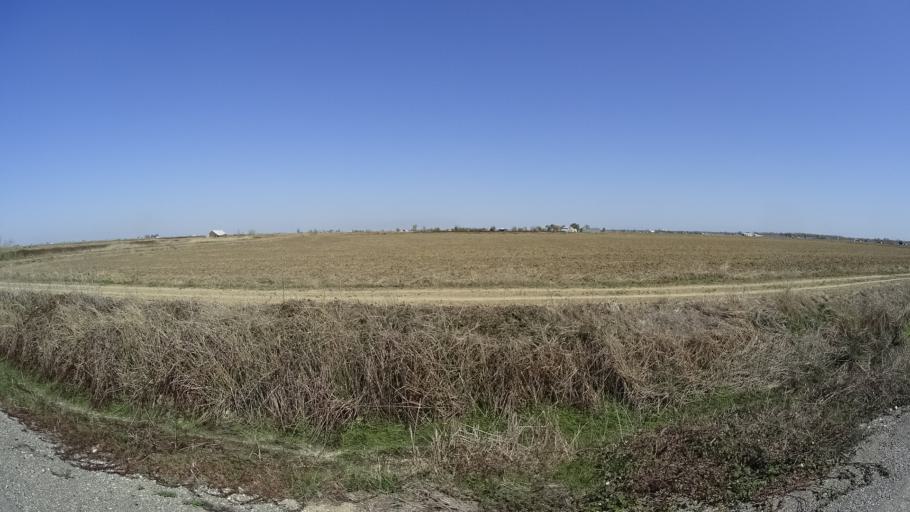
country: US
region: California
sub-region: Glenn County
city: Willows
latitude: 39.4285
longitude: -122.0442
